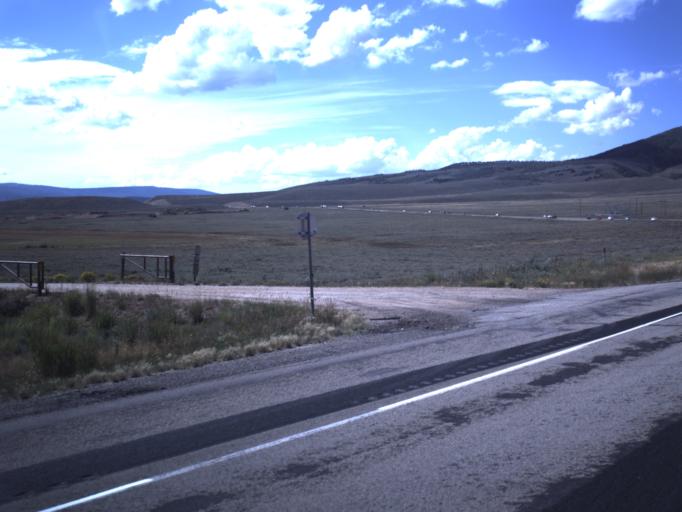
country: US
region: Utah
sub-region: Wasatch County
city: Heber
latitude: 40.2194
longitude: -111.1041
